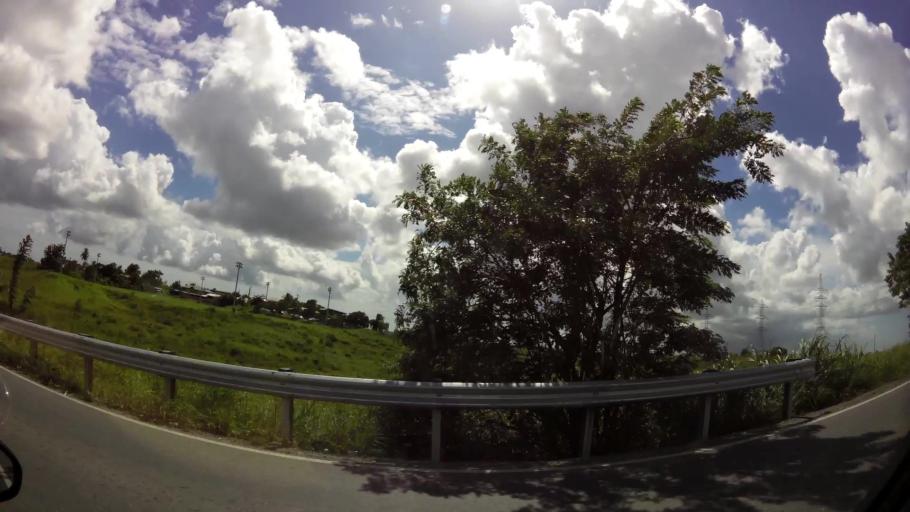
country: TT
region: Penal/Debe
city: Debe
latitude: 10.2179
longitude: -61.4599
